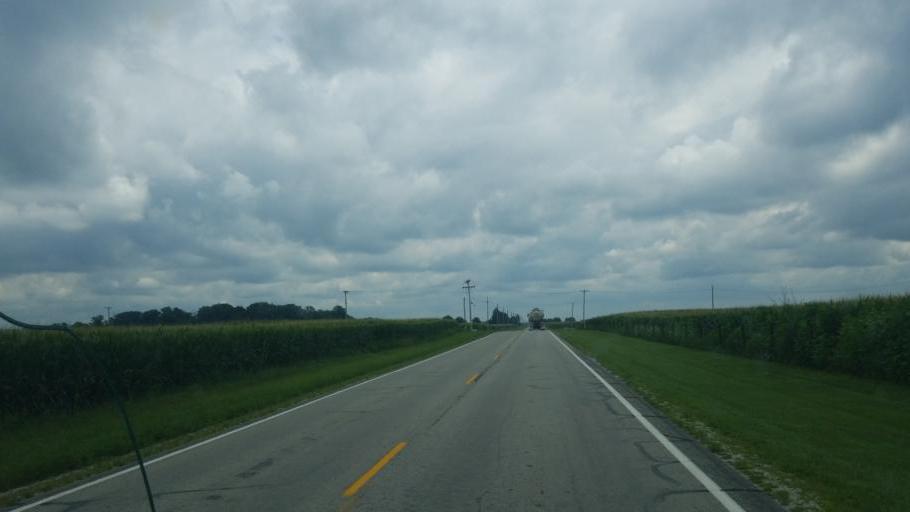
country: US
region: Indiana
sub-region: Wells County
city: Bluffton
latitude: 40.6546
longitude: -85.2046
